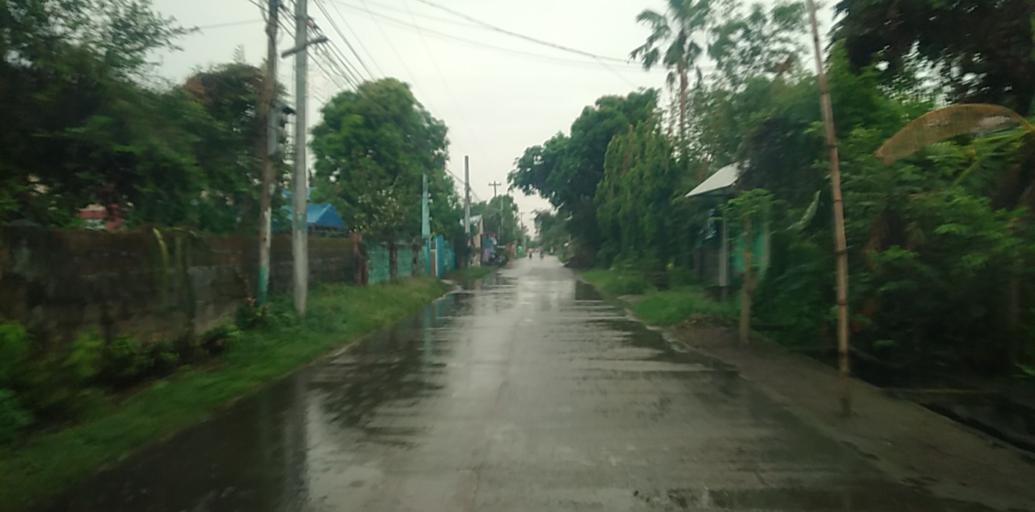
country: PH
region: Central Luzon
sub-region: Province of Pampanga
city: Arenas
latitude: 15.1683
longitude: 120.6868
